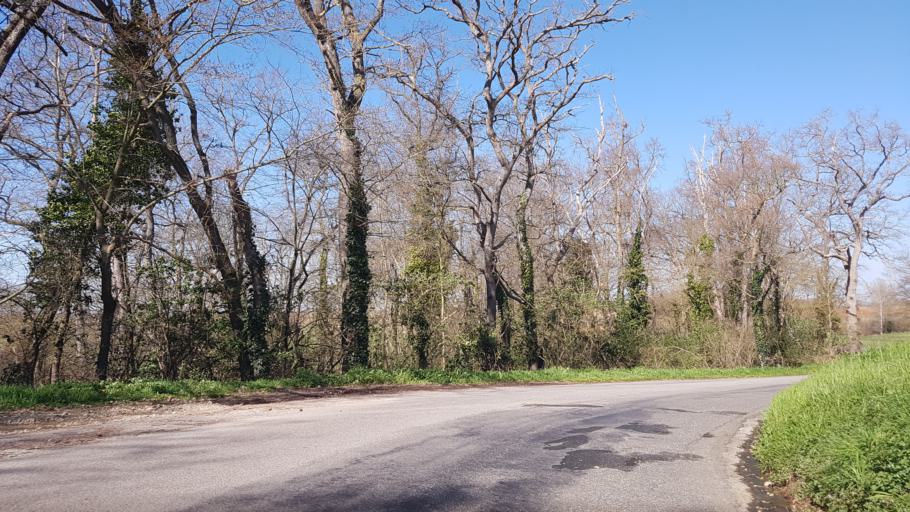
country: FR
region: Languedoc-Roussillon
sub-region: Departement de l'Aude
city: Belpech
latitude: 43.1812
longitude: 1.7054
